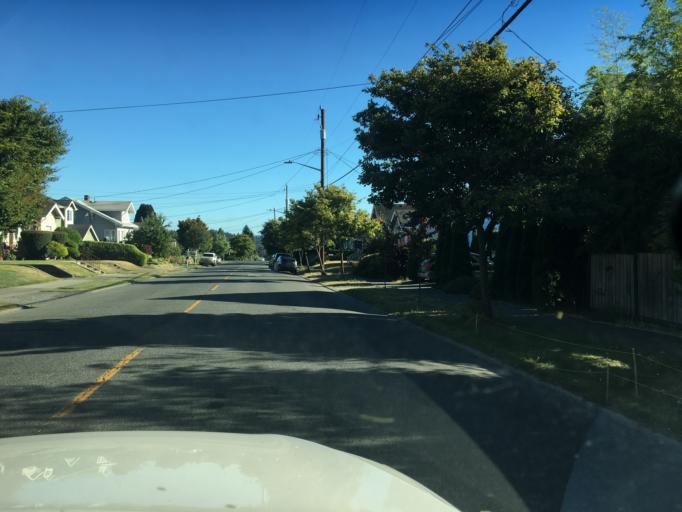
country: US
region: Washington
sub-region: King County
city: Shoreline
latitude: 47.6846
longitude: -122.3983
